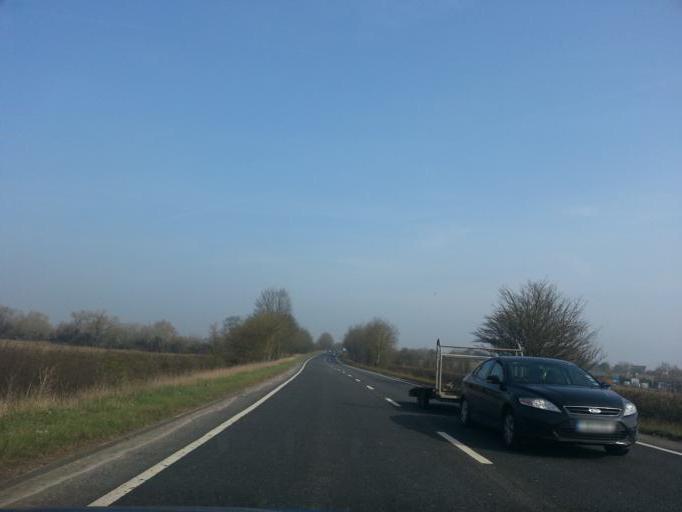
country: GB
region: England
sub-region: Oxfordshire
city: Shrivenham
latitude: 51.5928
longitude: -1.6717
